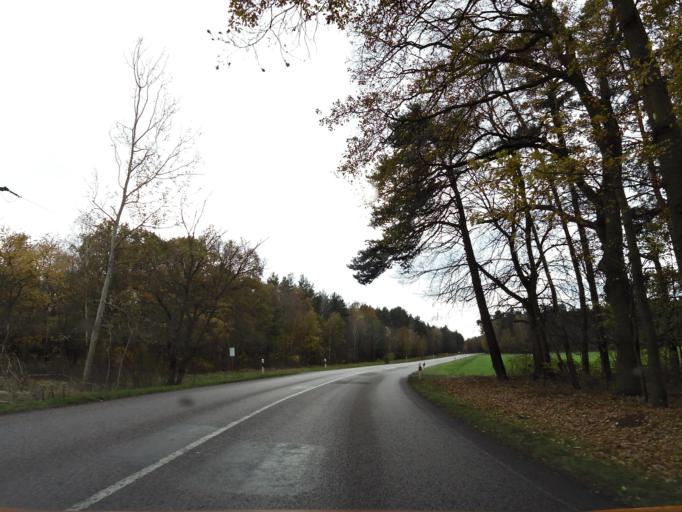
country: DE
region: Saxony-Anhalt
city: Haldensleben I
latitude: 52.3522
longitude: 11.4644
